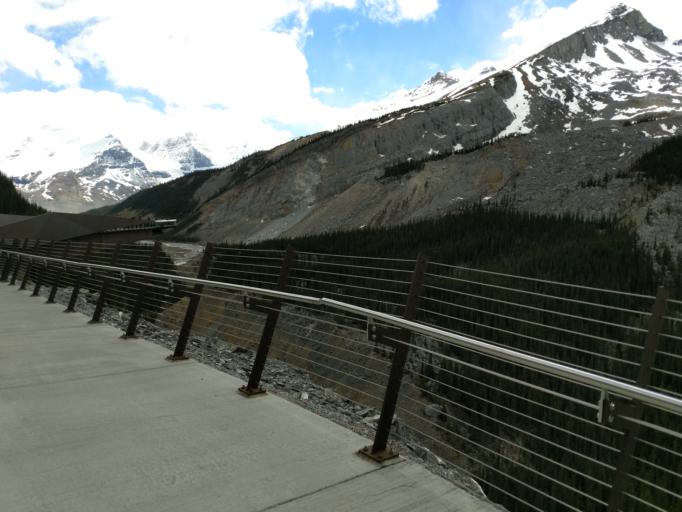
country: CA
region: Alberta
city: Jasper Park Lodge
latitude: 52.2595
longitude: -117.2779
